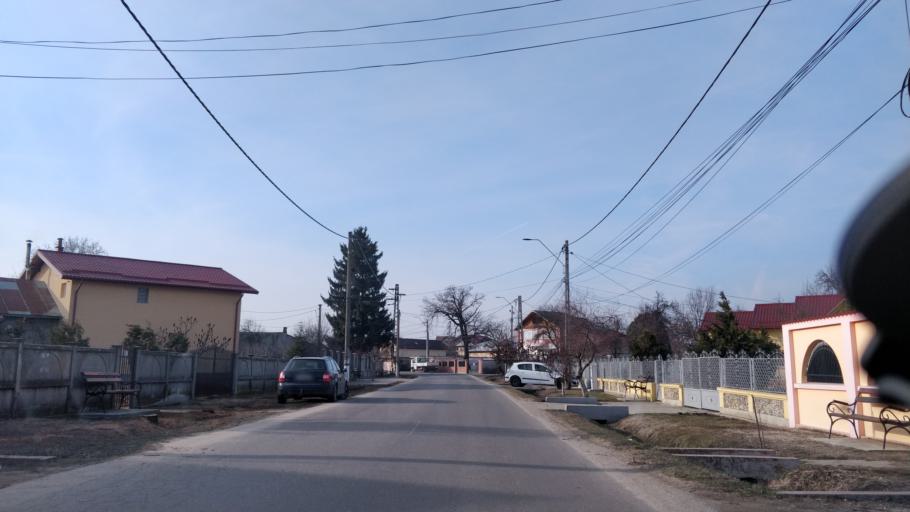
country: RO
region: Giurgiu
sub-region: Comuna Ulmi
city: Ulmi
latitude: 44.4824
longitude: 25.8047
